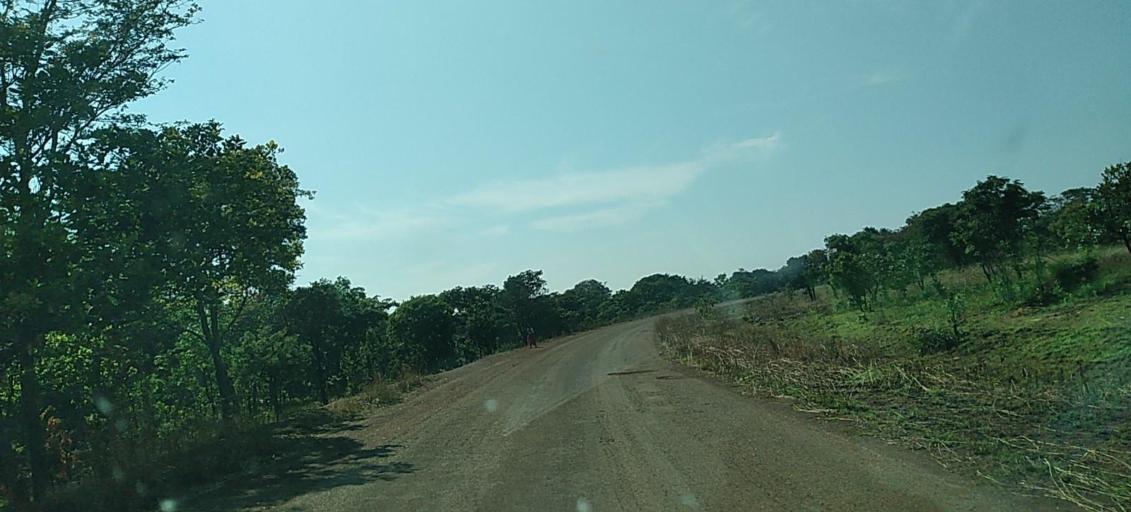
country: ZM
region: North-Western
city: Mwinilunga
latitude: -11.7920
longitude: 25.0696
